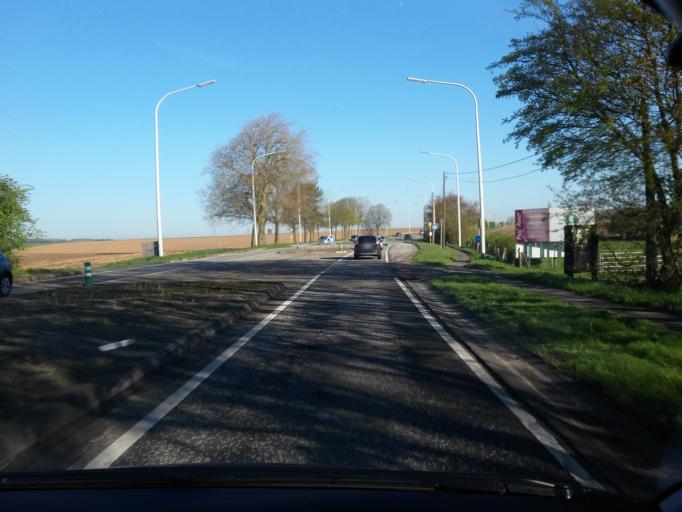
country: BE
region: Wallonia
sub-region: Province du Brabant Wallon
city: Genappe
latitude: 50.6390
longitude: 4.4240
